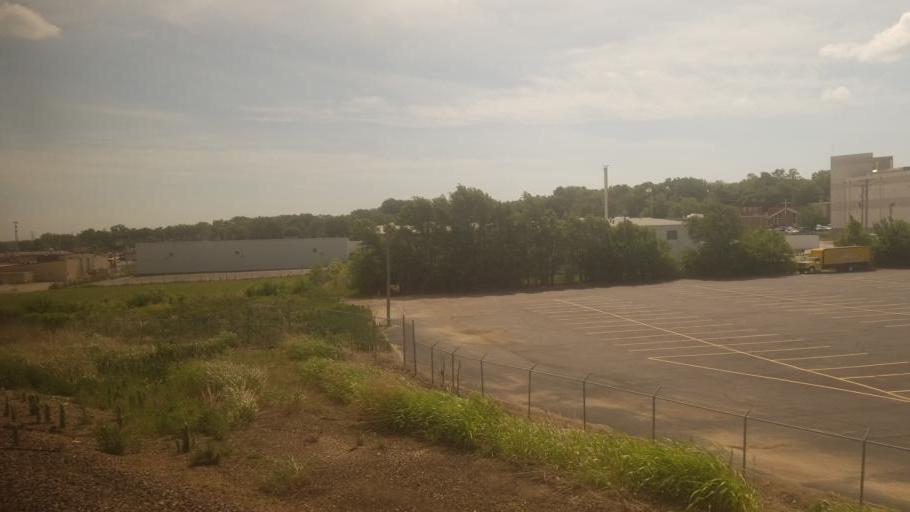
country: US
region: Missouri
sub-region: Clay County
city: North Kansas City
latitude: 39.1035
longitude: -94.5155
